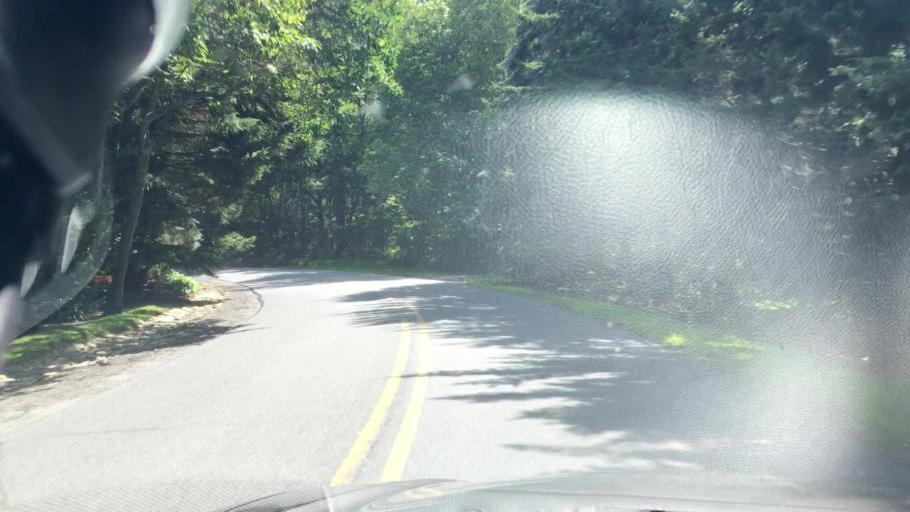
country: US
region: Pennsylvania
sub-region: Luzerne County
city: Oakdale
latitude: 41.0190
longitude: -75.9275
